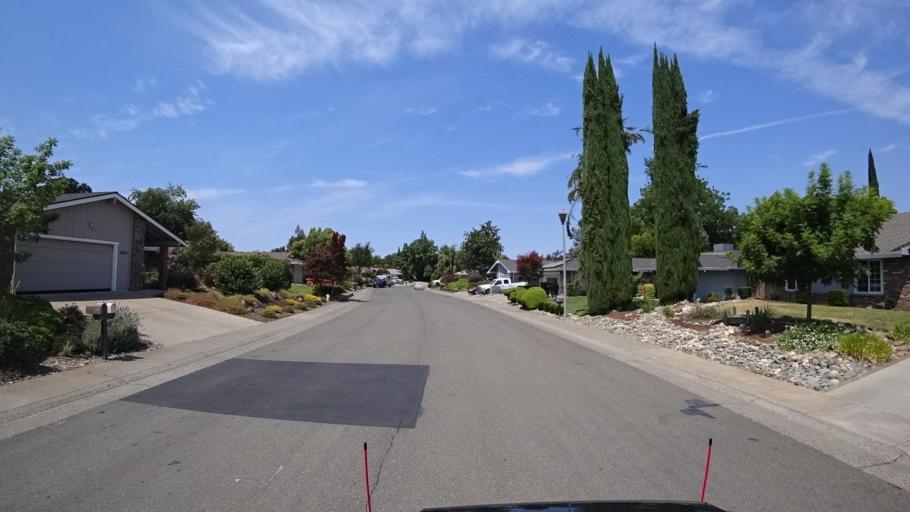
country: US
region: California
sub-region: Placer County
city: Rocklin
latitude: 38.7963
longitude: -121.2405
